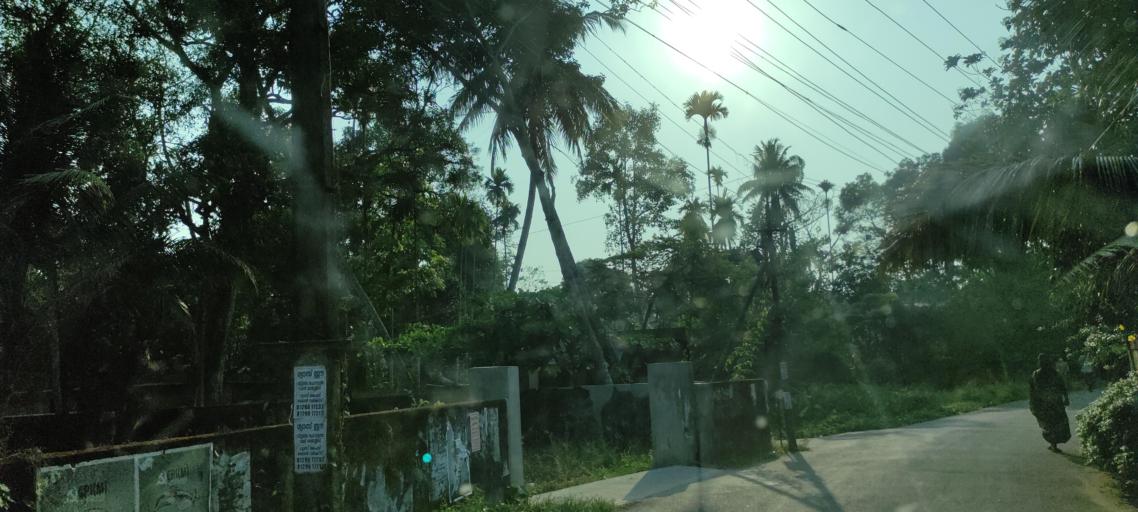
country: IN
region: Kerala
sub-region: Alappuzha
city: Alleppey
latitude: 9.5288
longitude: 76.3174
